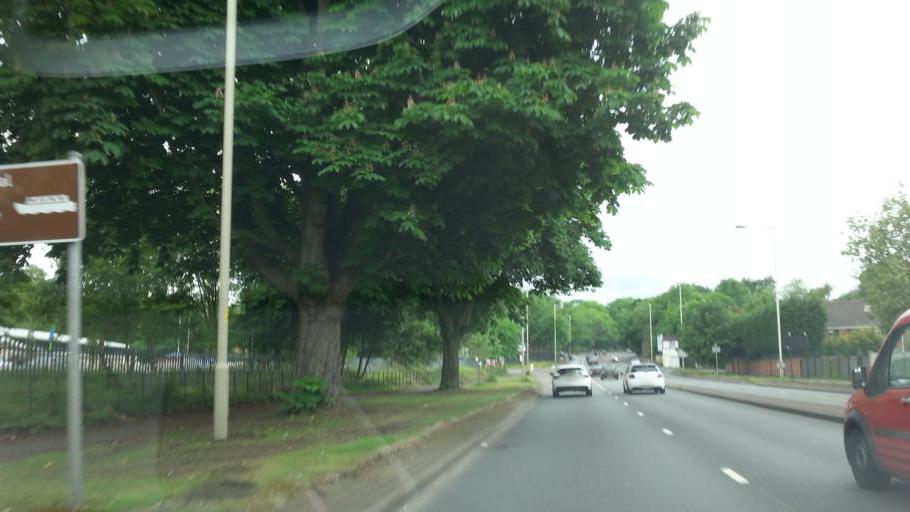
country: GB
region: England
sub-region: Sandwell
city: Tipton
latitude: 52.5242
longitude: -2.0769
